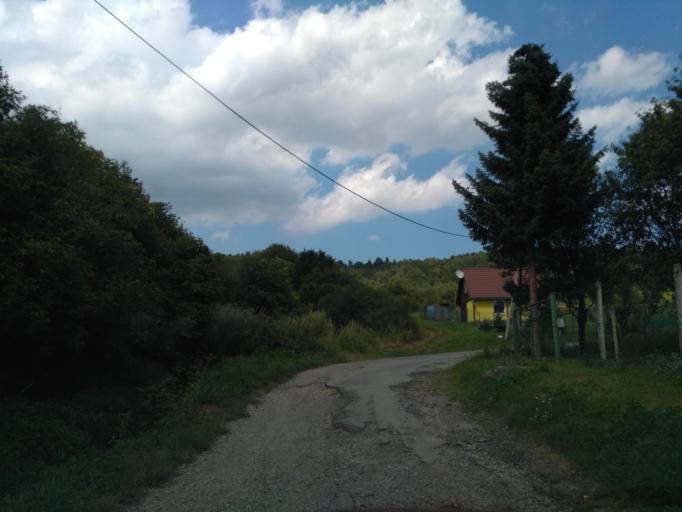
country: SK
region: Presovsky
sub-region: Okres Presov
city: Presov
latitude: 48.9160
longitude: 21.1685
